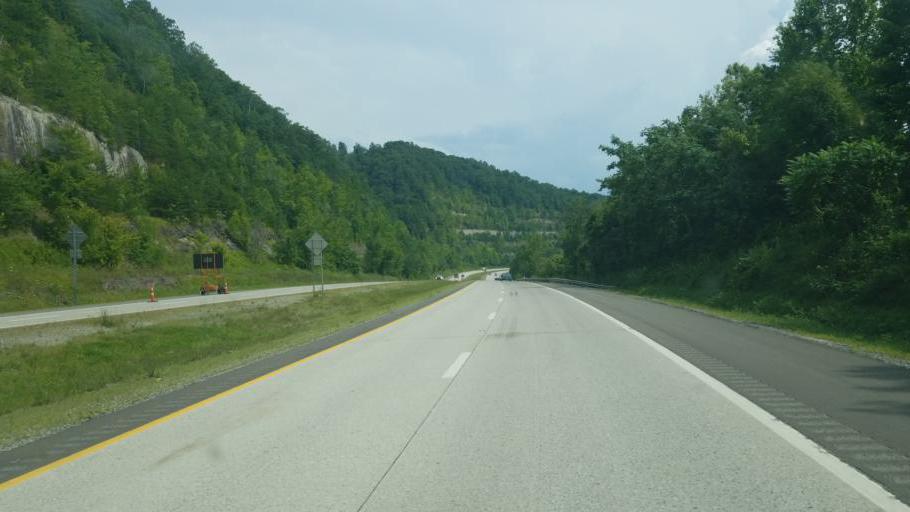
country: US
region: West Virginia
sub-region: Kanawha County
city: Alum Creek
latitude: 38.2179
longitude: -81.8338
